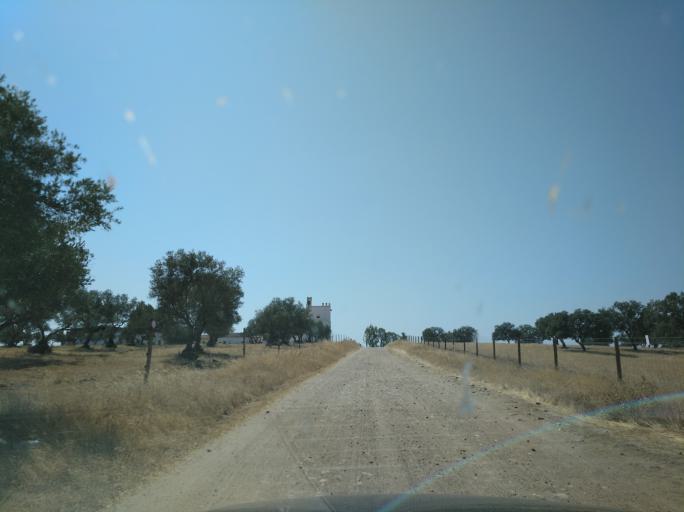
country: PT
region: Portalegre
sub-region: Campo Maior
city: Campo Maior
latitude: 39.0230
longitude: -6.9783
